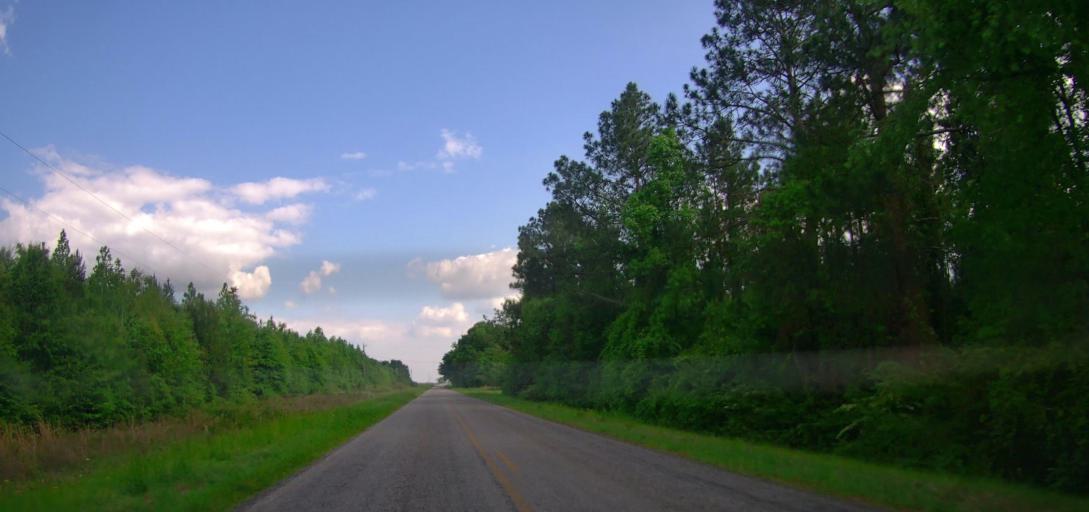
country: US
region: Georgia
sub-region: Laurens County
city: East Dublin
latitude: 32.6908
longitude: -82.9000
